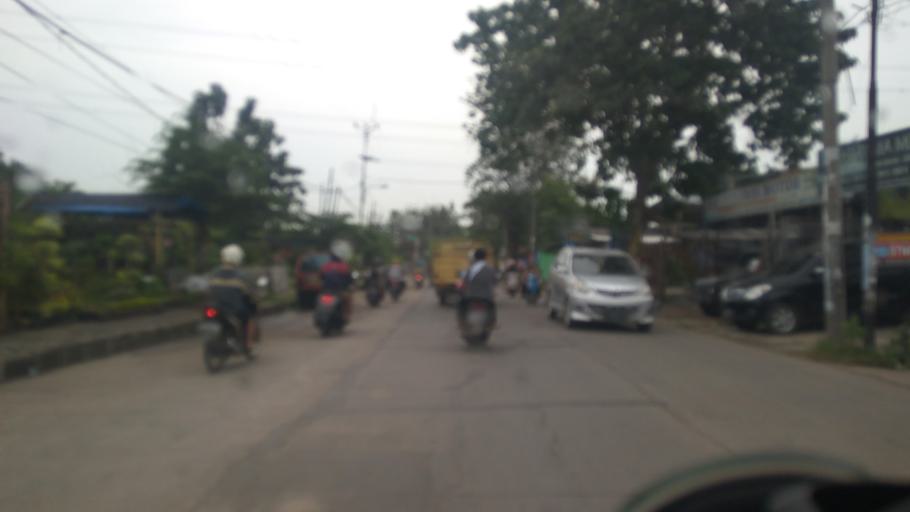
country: ID
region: West Java
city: Bekasi
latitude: -6.2063
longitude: 107.0316
